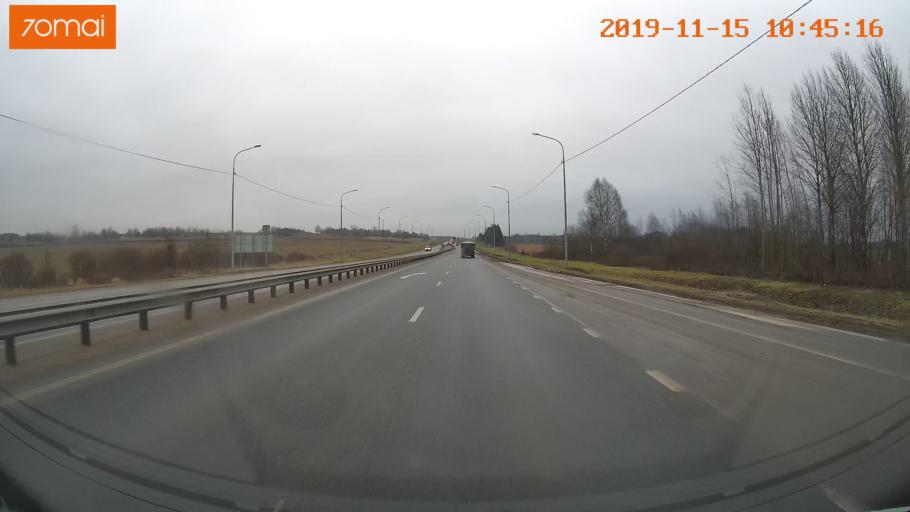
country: RU
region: Vologda
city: Sheksna
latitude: 59.2111
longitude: 38.5827
